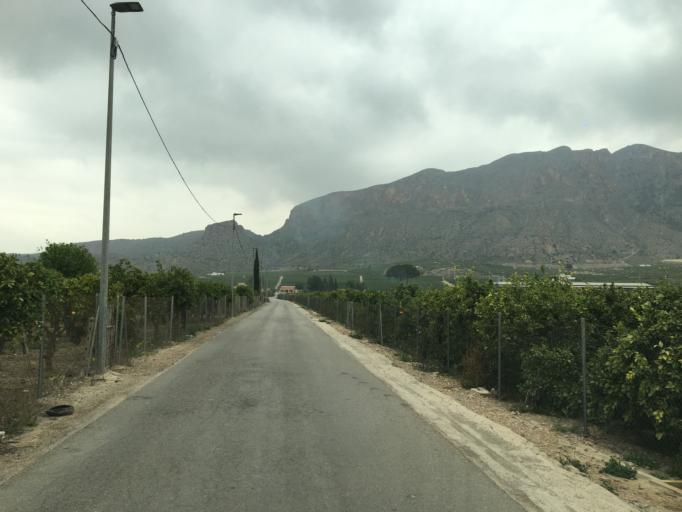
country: ES
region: Murcia
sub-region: Murcia
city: Santomera
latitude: 38.0715
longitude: -1.0285
